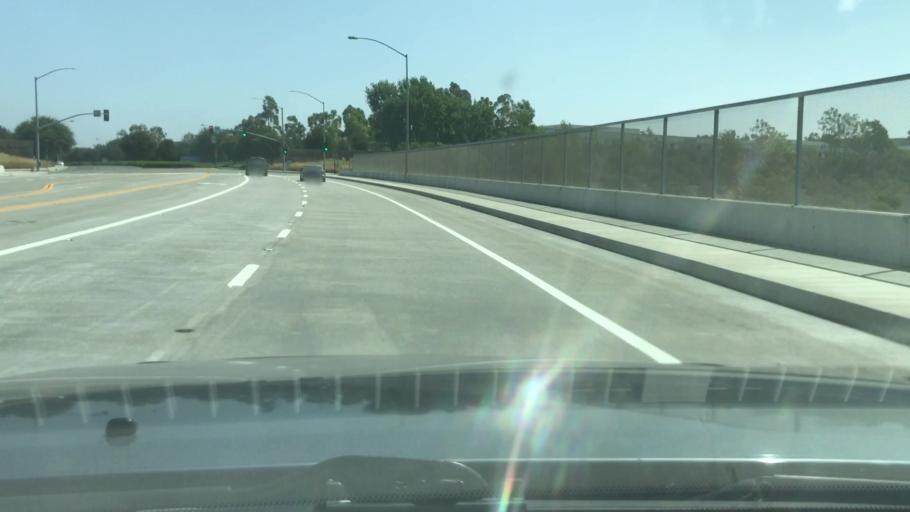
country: US
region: California
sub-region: Orange County
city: San Joaquin Hills
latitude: 33.6375
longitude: -117.8567
